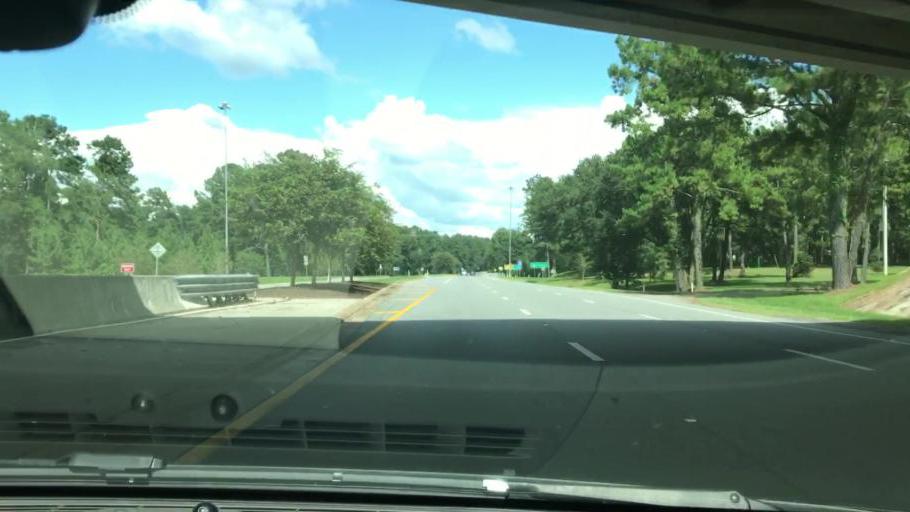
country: US
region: Florida
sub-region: Leon County
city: Tallahassee
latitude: 30.4884
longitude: -84.1578
